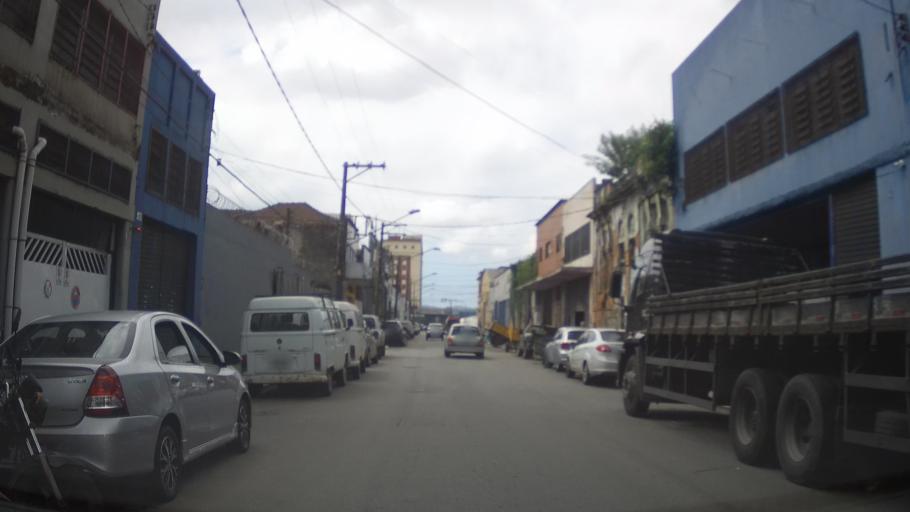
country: BR
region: Sao Paulo
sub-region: Santos
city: Santos
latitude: -23.9375
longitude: -46.3200
